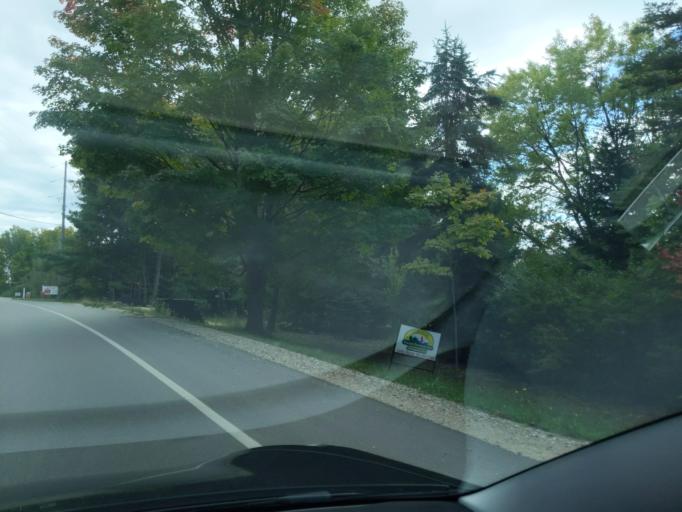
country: US
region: Michigan
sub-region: Kalkaska County
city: Rapid City
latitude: 44.9018
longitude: -85.2805
